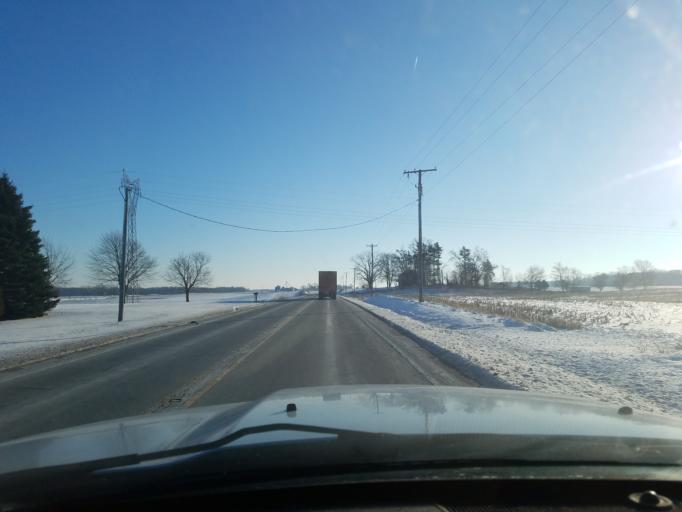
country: US
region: Indiana
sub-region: Noble County
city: Albion
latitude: 41.4531
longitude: -85.4526
